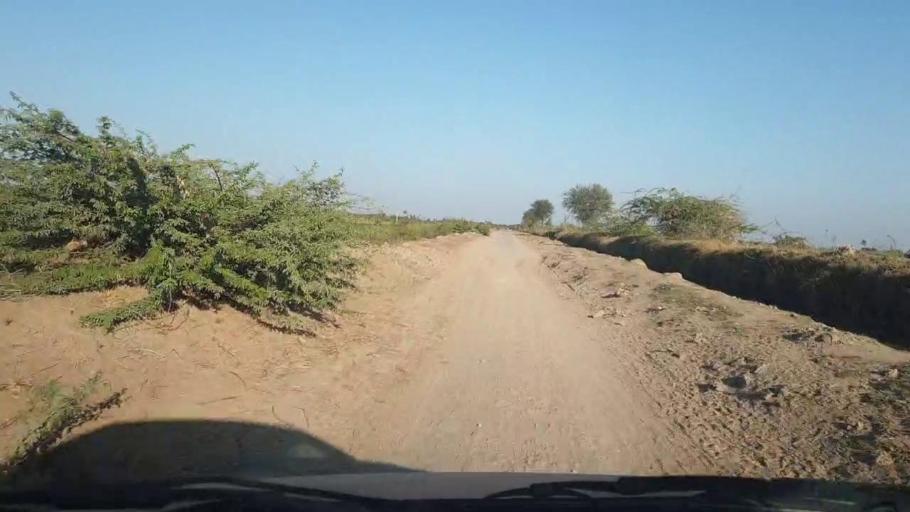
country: PK
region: Sindh
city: Samaro
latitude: 25.3266
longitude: 69.3126
